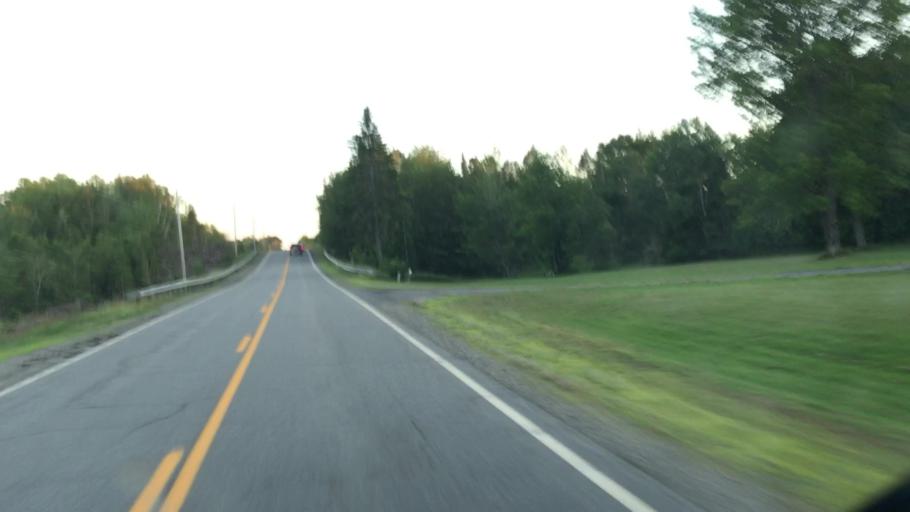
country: US
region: Maine
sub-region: Penobscot County
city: Medway
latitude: 45.6032
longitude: -68.3084
